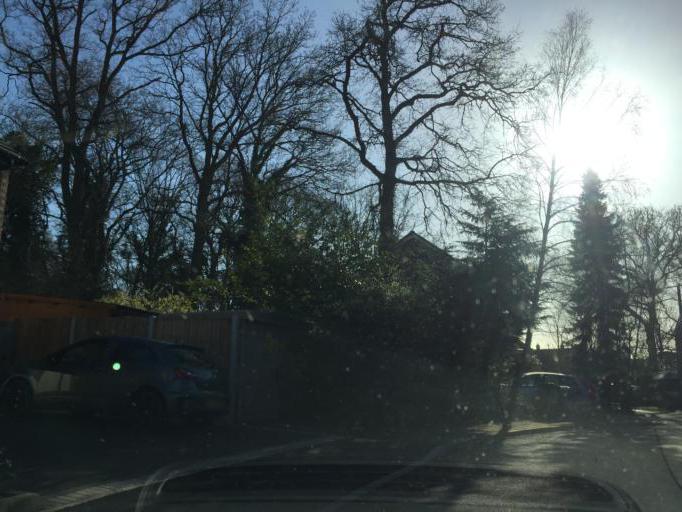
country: GB
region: England
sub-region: Warwickshire
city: Harbury
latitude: 52.1982
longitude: -1.4845
